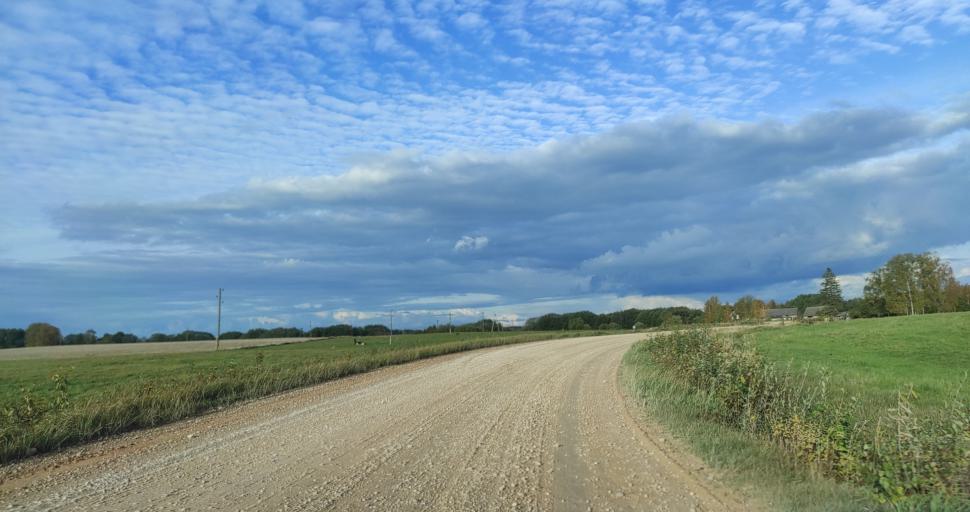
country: LV
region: Aizpute
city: Aizpute
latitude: 56.7488
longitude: 21.7923
